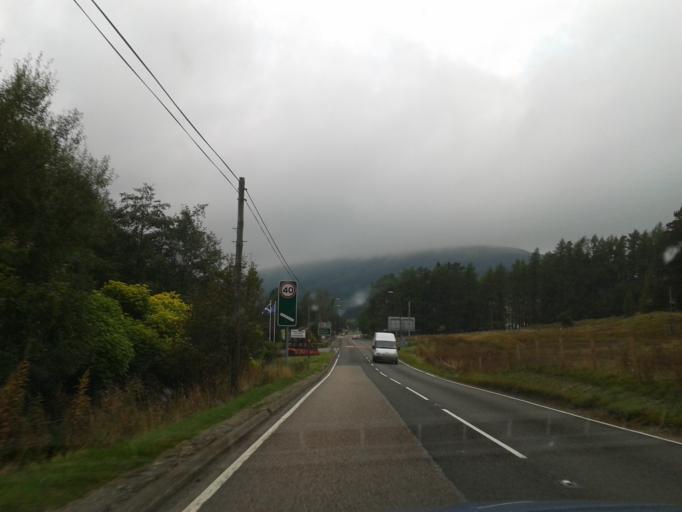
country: GB
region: Scotland
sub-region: Argyll and Bute
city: Garelochhead
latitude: 56.4332
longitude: -4.7069
